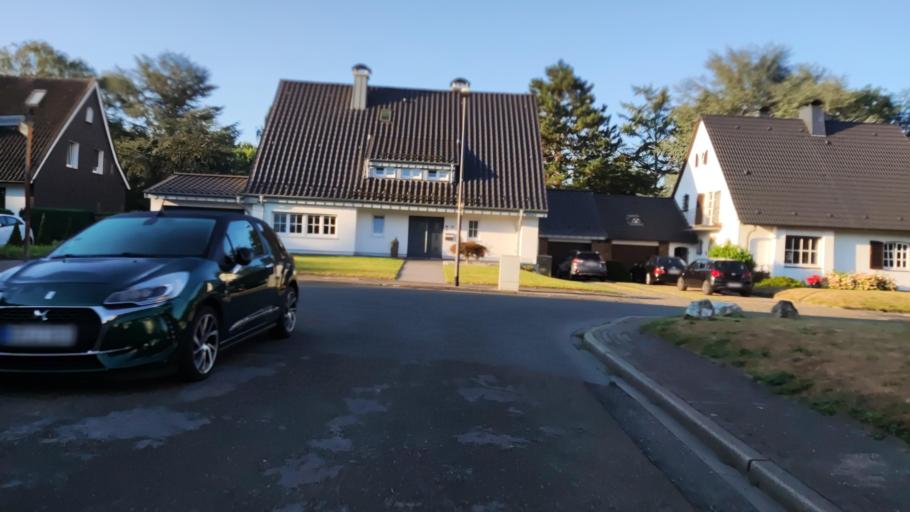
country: DE
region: North Rhine-Westphalia
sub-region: Regierungsbezirk Arnsberg
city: Herne
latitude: 51.5392
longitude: 7.2375
